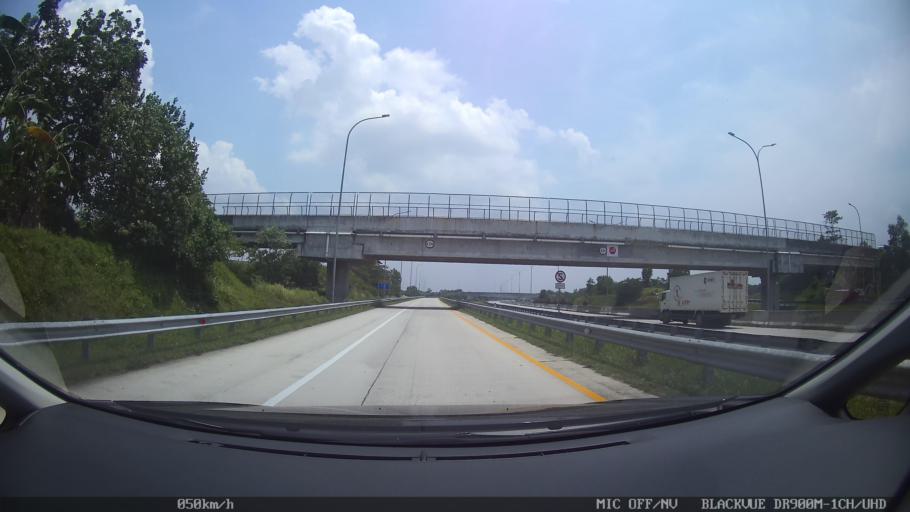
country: ID
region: Lampung
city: Natar
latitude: -5.2777
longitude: 105.2162
